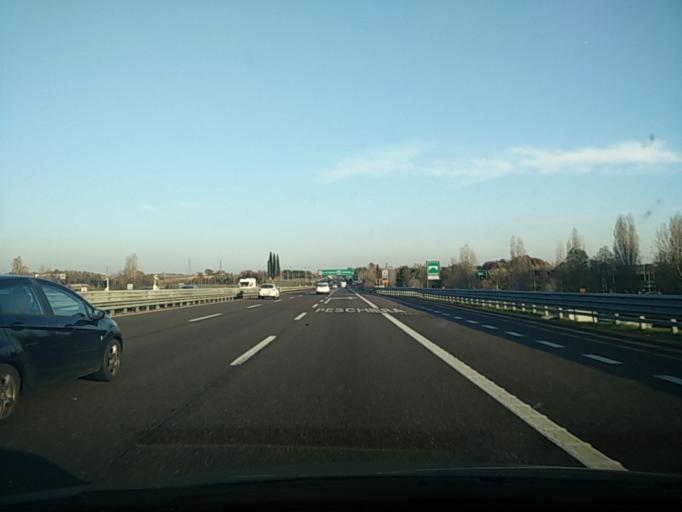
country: IT
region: Veneto
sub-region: Provincia di Verona
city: Peschiera del Garda
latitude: 45.4292
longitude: 10.6987
